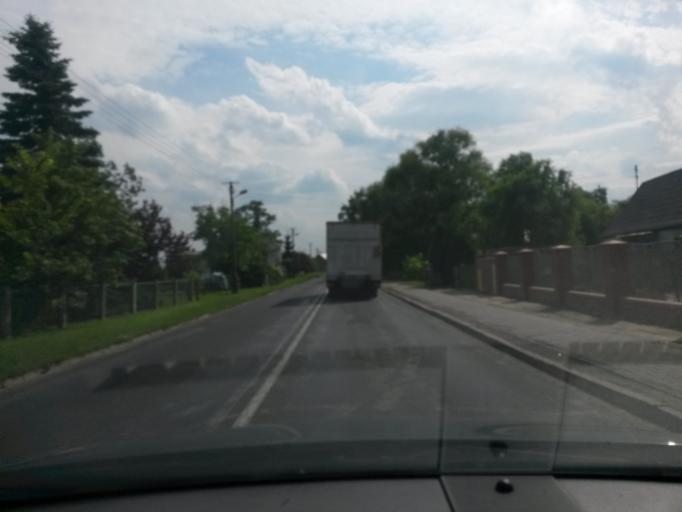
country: PL
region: Greater Poland Voivodeship
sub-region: Powiat poznanski
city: Kleszczewo
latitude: 52.3057
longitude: 17.1307
